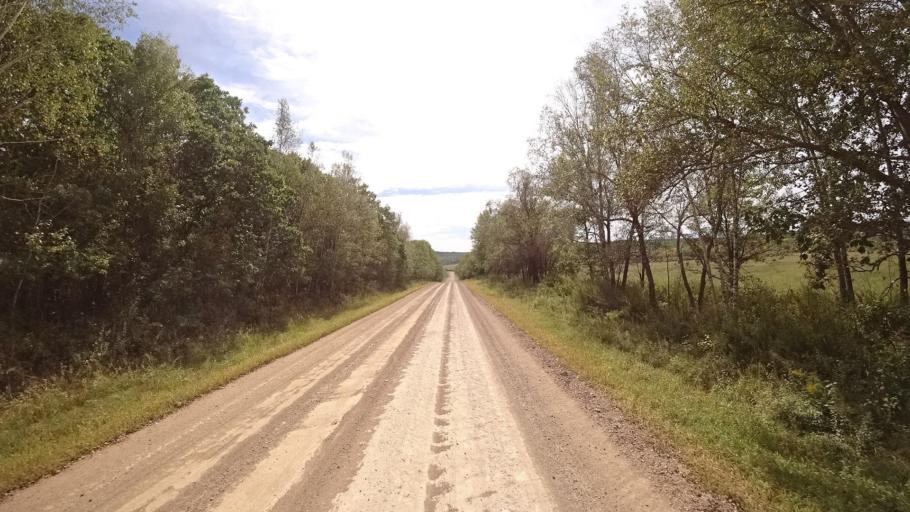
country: RU
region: Primorskiy
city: Yakovlevka
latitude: 44.6253
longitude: 133.5997
